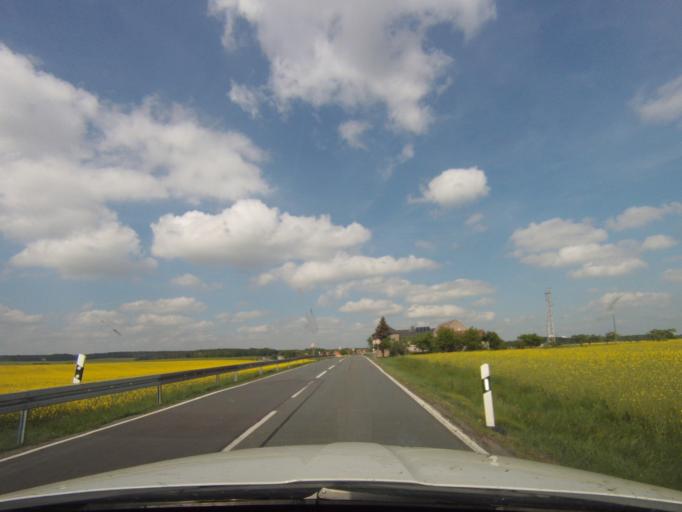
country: DE
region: Thuringia
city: Mittelpollnitz
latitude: 50.7618
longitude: 11.9224
